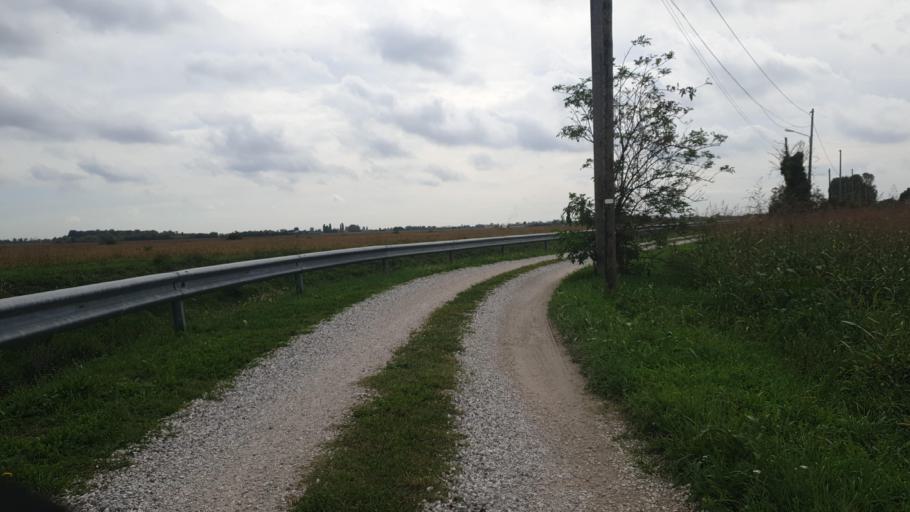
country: IT
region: Veneto
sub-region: Provincia di Padova
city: Ponte San Nicolo
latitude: 45.3438
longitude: 11.9194
